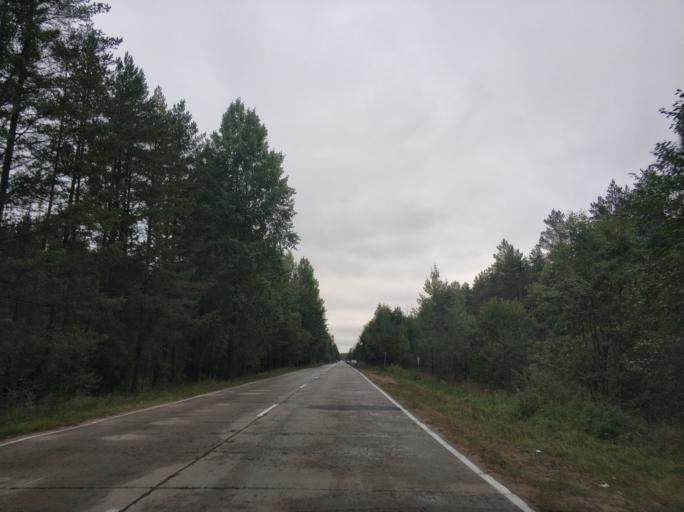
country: RU
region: Leningrad
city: Borisova Griva
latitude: 60.1748
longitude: 30.9193
